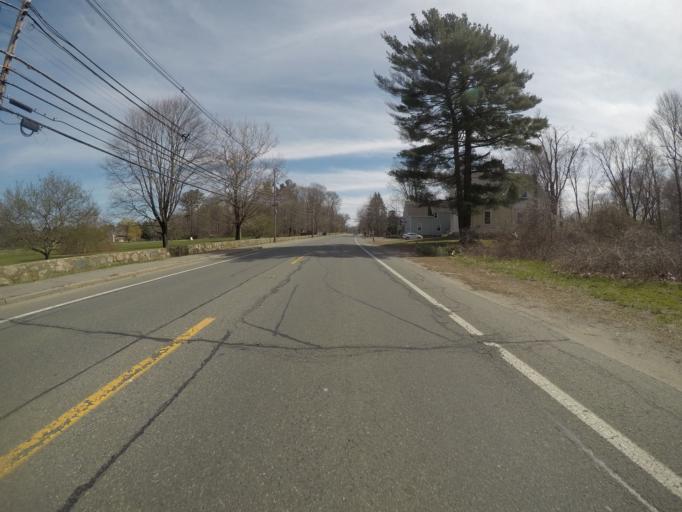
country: US
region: Massachusetts
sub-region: Bristol County
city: Easton
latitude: 42.0535
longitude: -71.0851
